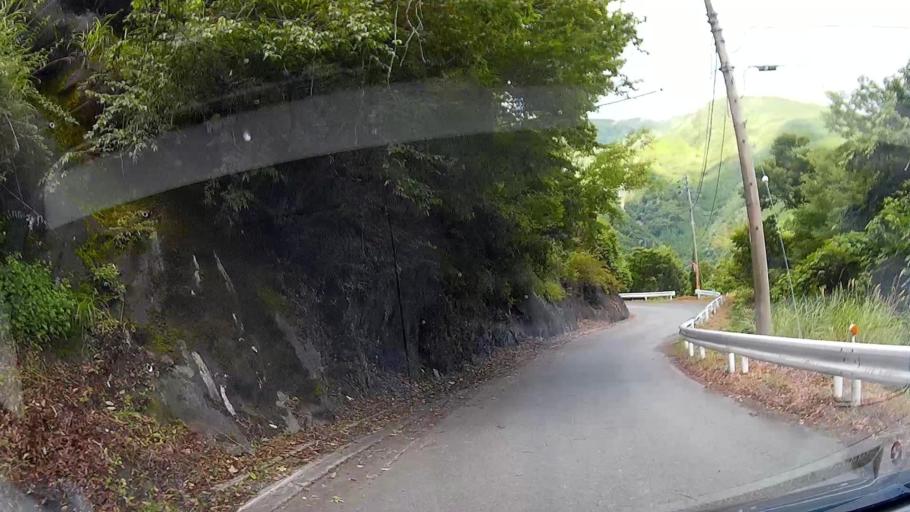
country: JP
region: Shizuoka
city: Shizuoka-shi
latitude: 35.2910
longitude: 138.2174
